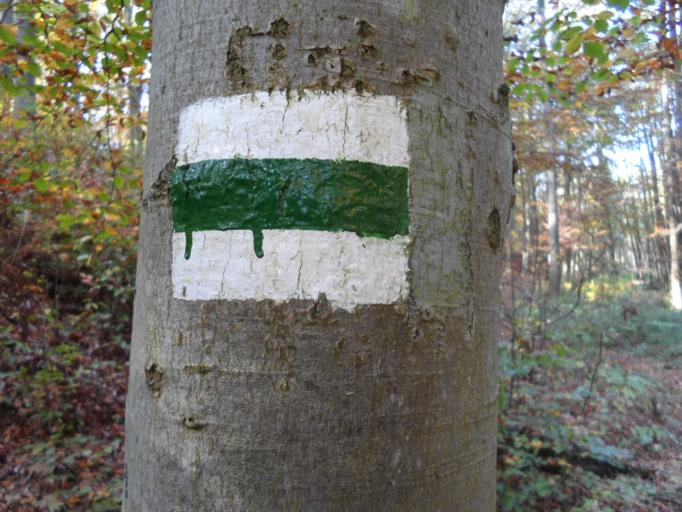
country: HU
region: Veszprem
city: Ajka
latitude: 47.2025
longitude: 17.6129
